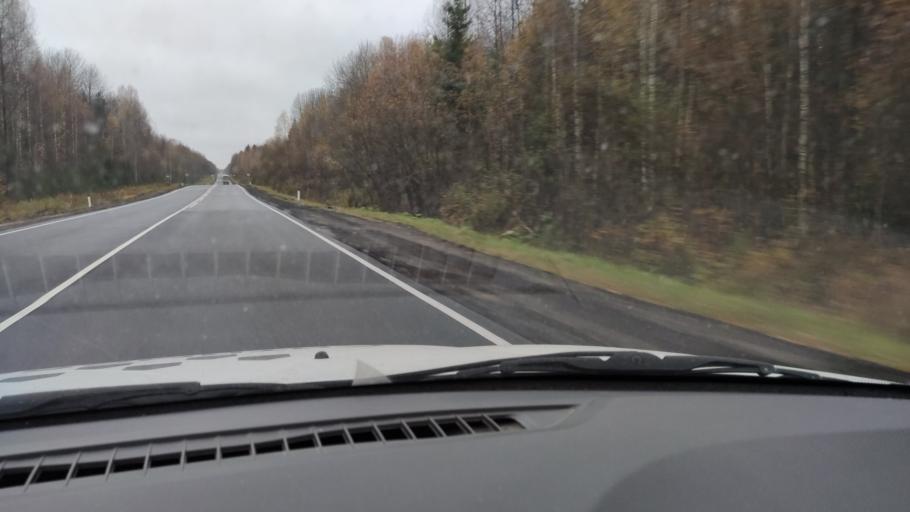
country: RU
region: Kirov
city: Omutninsk
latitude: 58.7620
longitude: 52.0033
